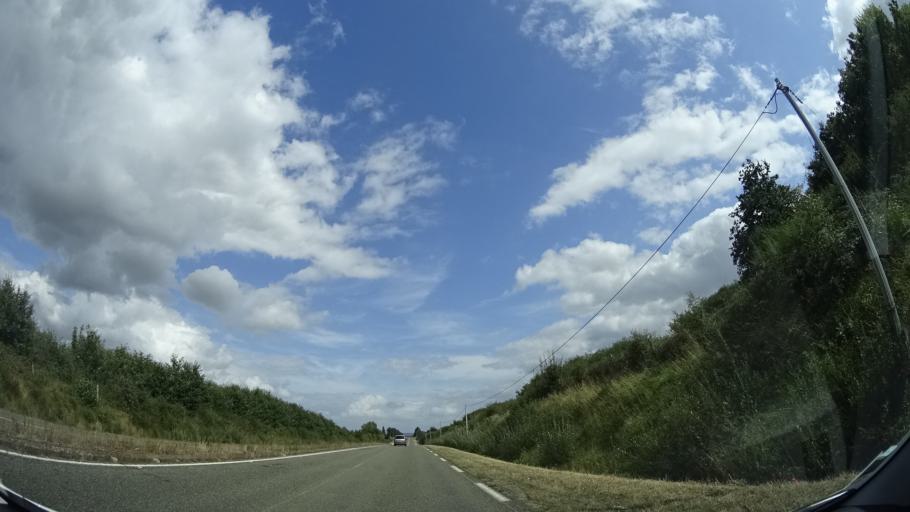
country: FR
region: Pays de la Loire
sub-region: Departement de la Mayenne
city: Vaiges
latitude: 48.0375
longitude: -0.4365
